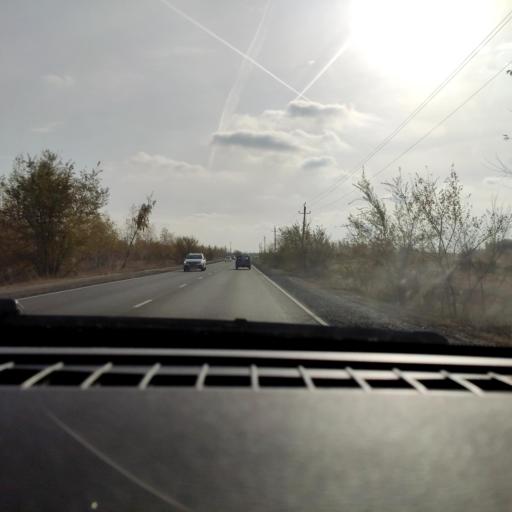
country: RU
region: Voronezj
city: Maslovka
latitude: 51.5805
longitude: 39.2626
